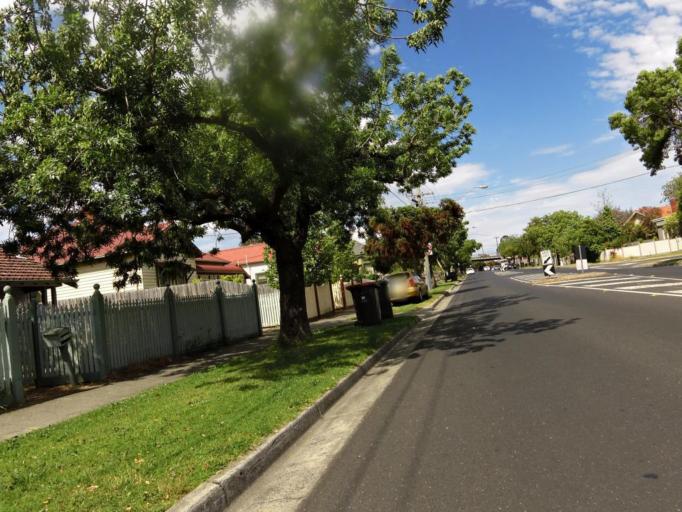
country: AU
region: Victoria
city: Hughesdale
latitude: -37.8989
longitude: 145.0850
